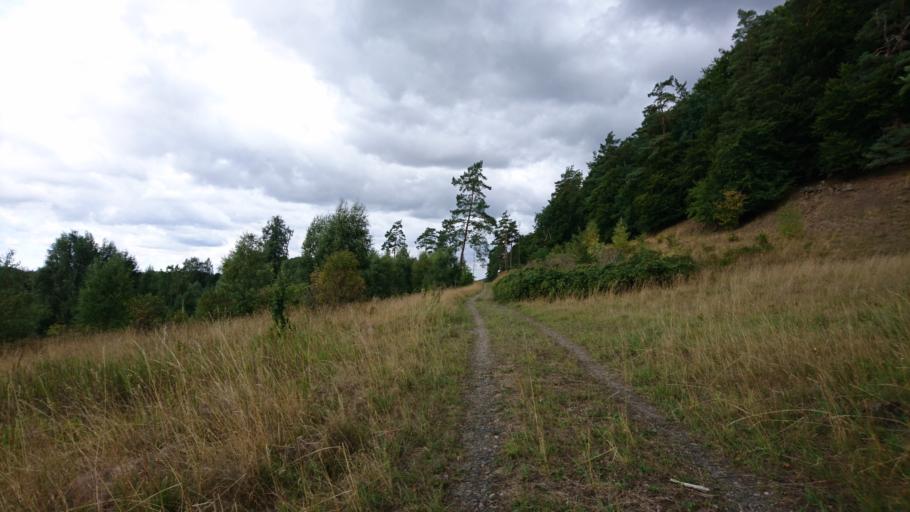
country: SE
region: Skane
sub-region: Sjobo Kommun
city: Sjoebo
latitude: 55.5922
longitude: 13.7708
